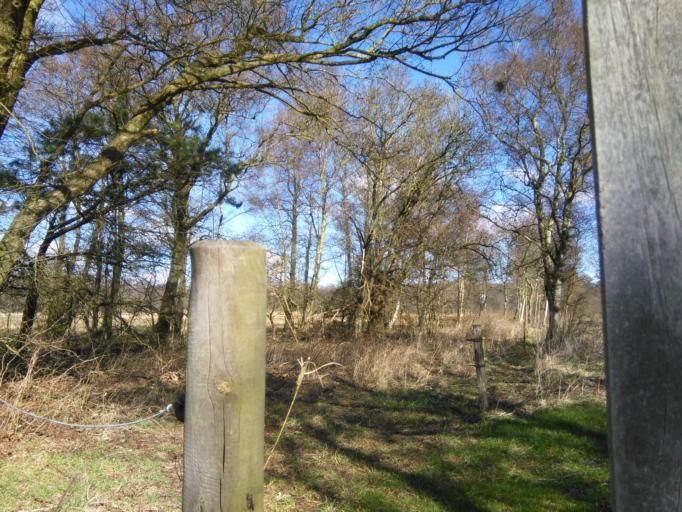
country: DK
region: Central Jutland
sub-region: Skanderborg Kommune
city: Ry
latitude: 56.0443
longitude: 9.7109
